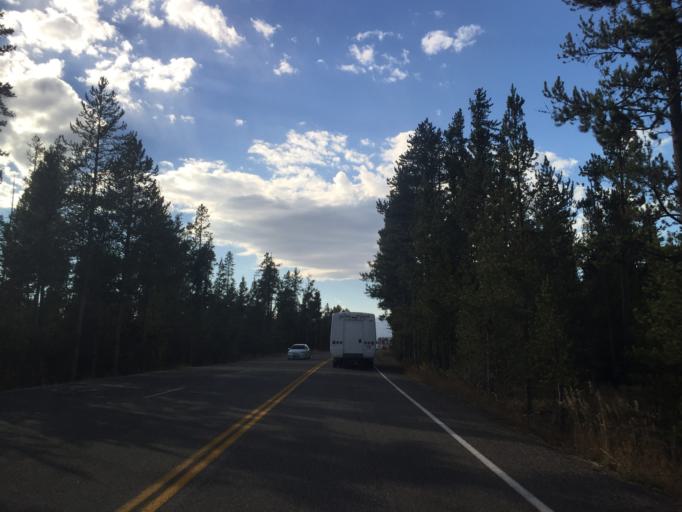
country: US
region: Montana
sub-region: Gallatin County
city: West Yellowstone
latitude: 44.6577
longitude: -111.0934
